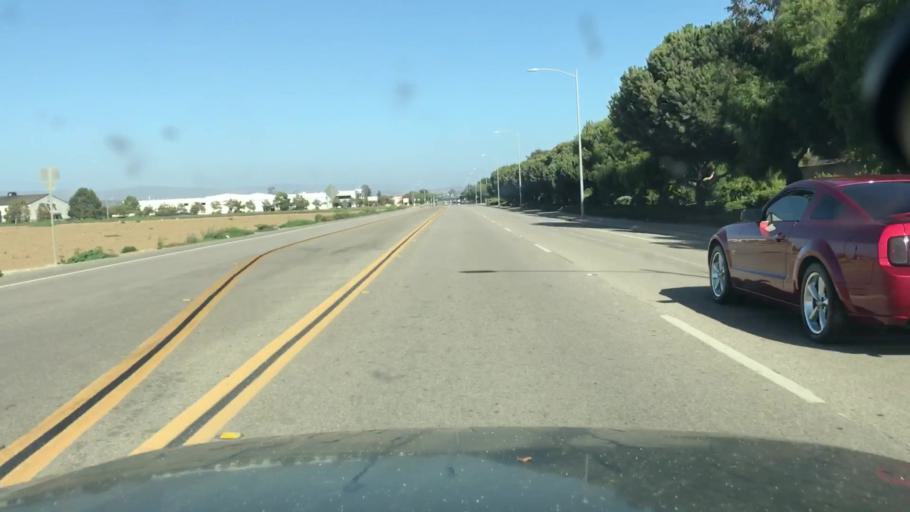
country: US
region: California
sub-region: Santa Barbara County
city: Lompoc
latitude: 34.6610
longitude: -120.4742
